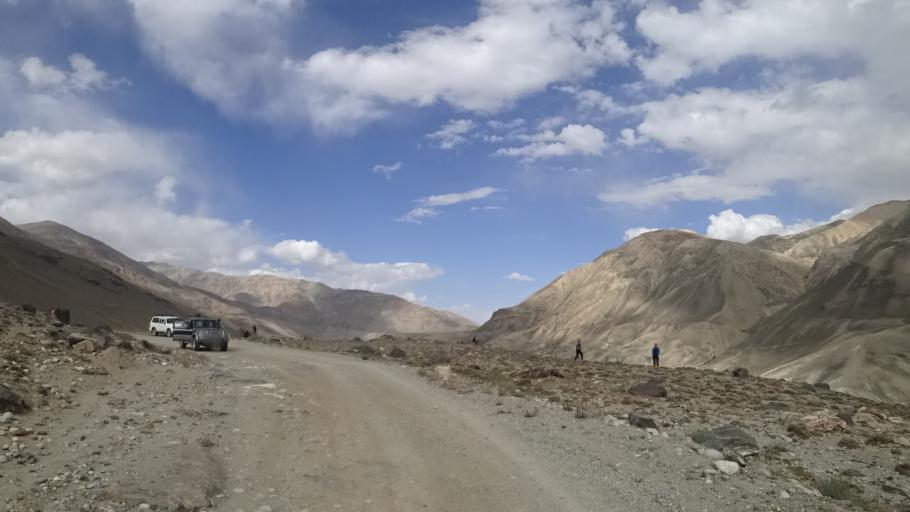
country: AF
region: Badakhshan
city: Khandud
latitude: 37.1988
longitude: 72.7729
